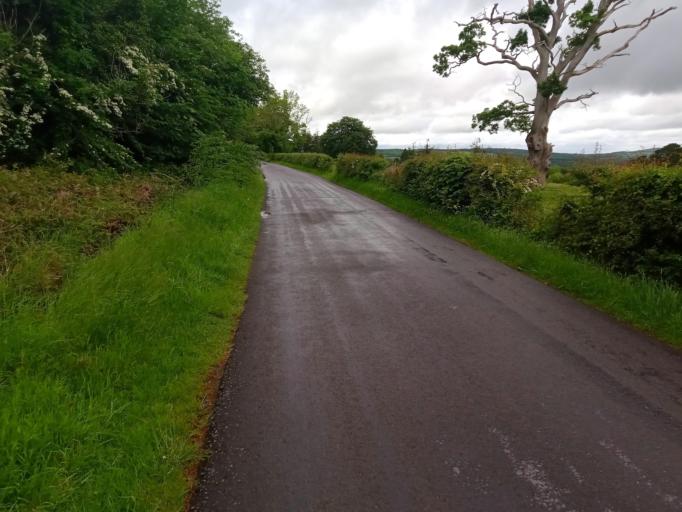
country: IE
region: Leinster
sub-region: Kilkenny
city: Thomastown
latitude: 52.4786
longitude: -7.0620
